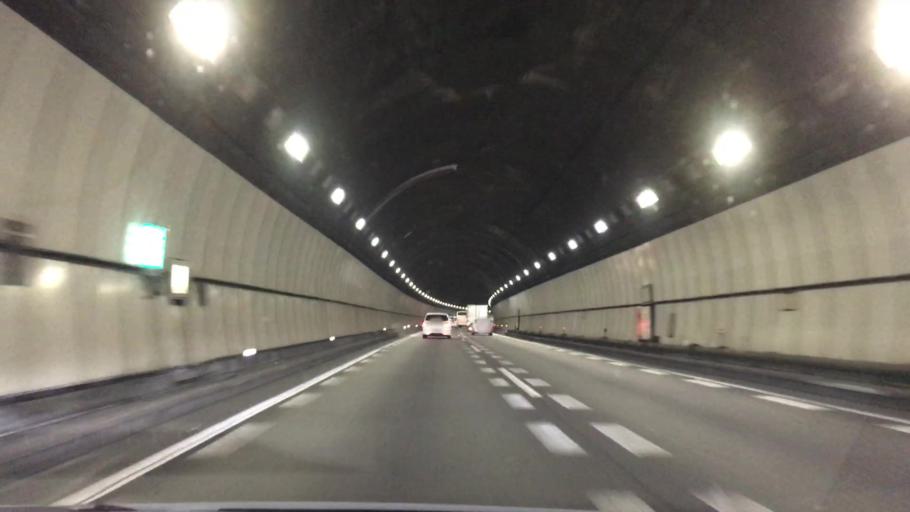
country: JP
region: Shizuoka
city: Shizuoka-shi
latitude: 35.0582
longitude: 138.5197
